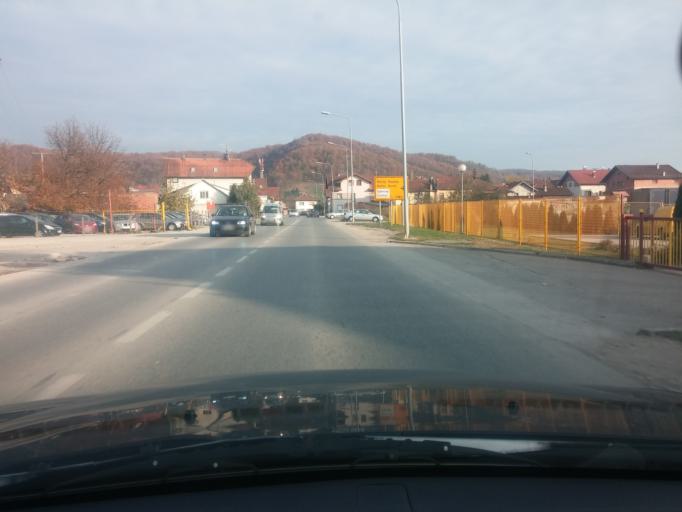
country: BA
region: Republika Srpska
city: Trn
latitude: 44.8178
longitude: 17.2116
